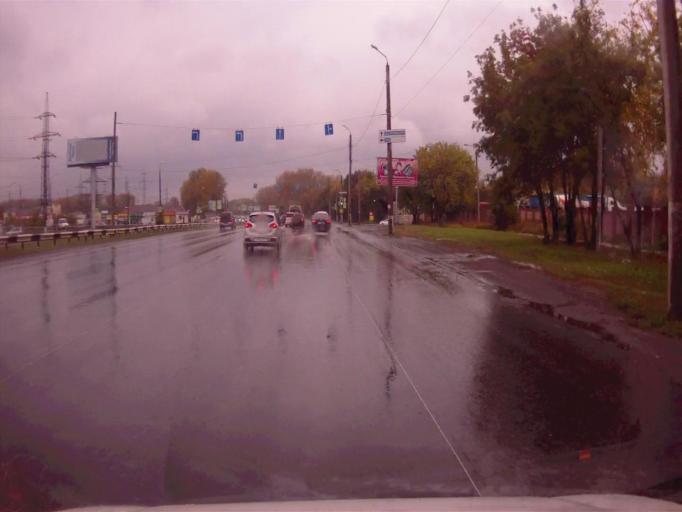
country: RU
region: Chelyabinsk
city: Dolgoderevenskoye
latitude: 55.2398
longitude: 61.3612
